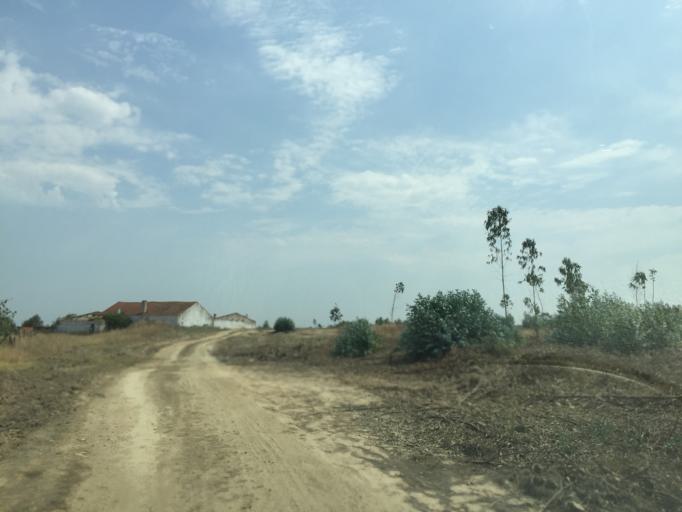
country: PT
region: Setubal
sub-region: Grandola
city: Grandola
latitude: 38.0516
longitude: -8.4544
